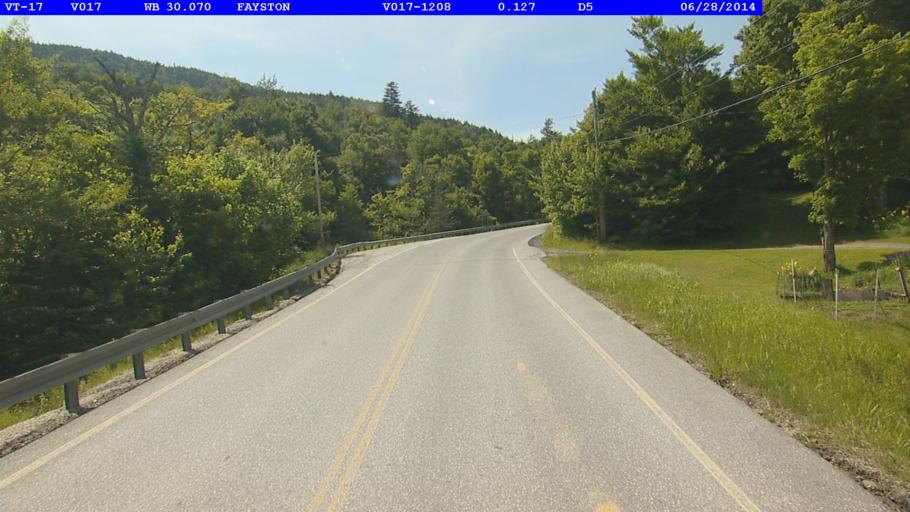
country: US
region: Vermont
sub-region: Addison County
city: Bristol
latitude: 44.2076
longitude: -72.9275
